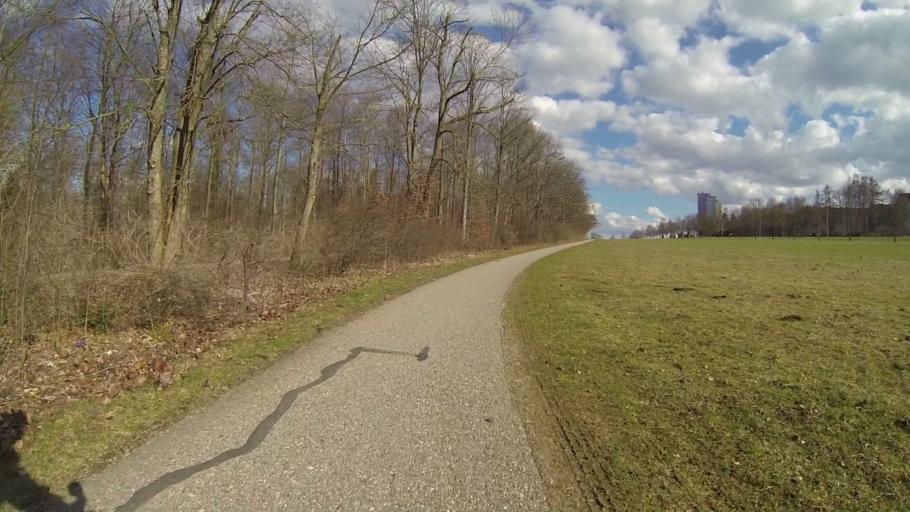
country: DE
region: Baden-Wuerttemberg
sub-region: Regierungsbezirk Stuttgart
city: Heidenheim an der Brenz
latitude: 48.6943
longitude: 10.1366
